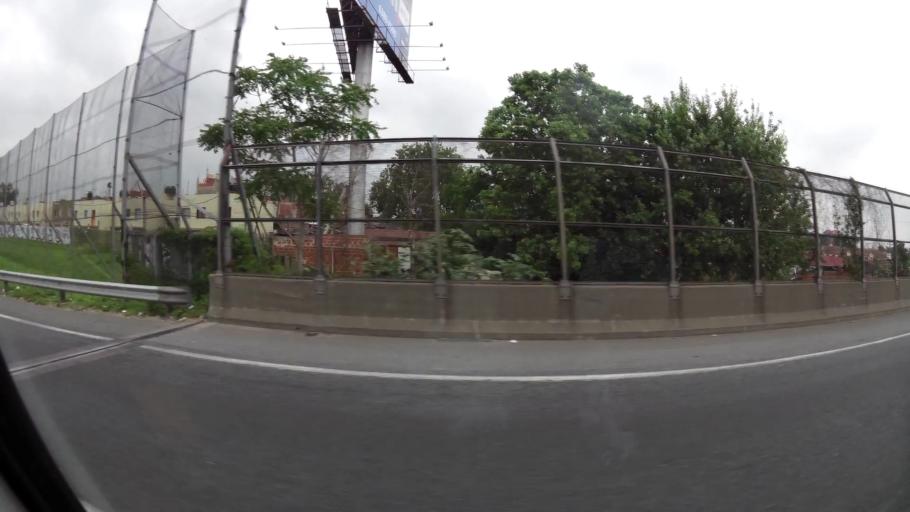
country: AR
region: Buenos Aires
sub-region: Partido de Avellaneda
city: Avellaneda
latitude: -34.6455
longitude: -58.3506
